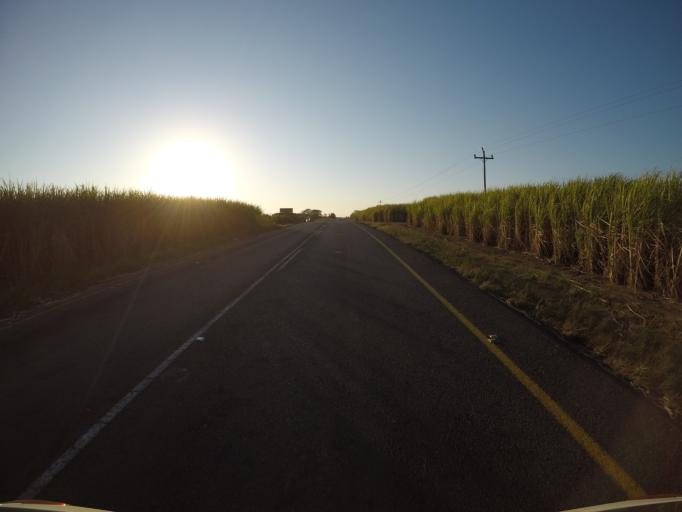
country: ZA
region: KwaZulu-Natal
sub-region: uThungulu District Municipality
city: eSikhawini
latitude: -28.9481
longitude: 31.7306
